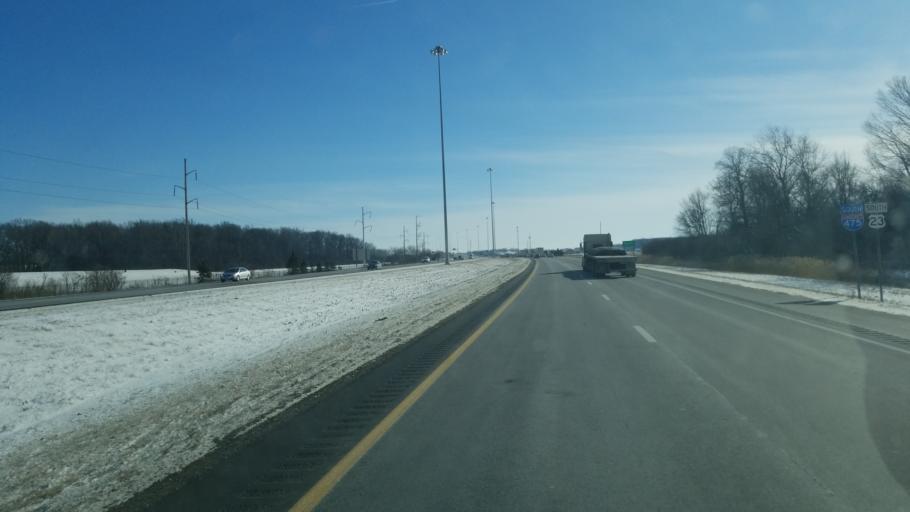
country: US
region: Ohio
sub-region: Lucas County
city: Maumee
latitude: 41.5710
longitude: -83.6913
